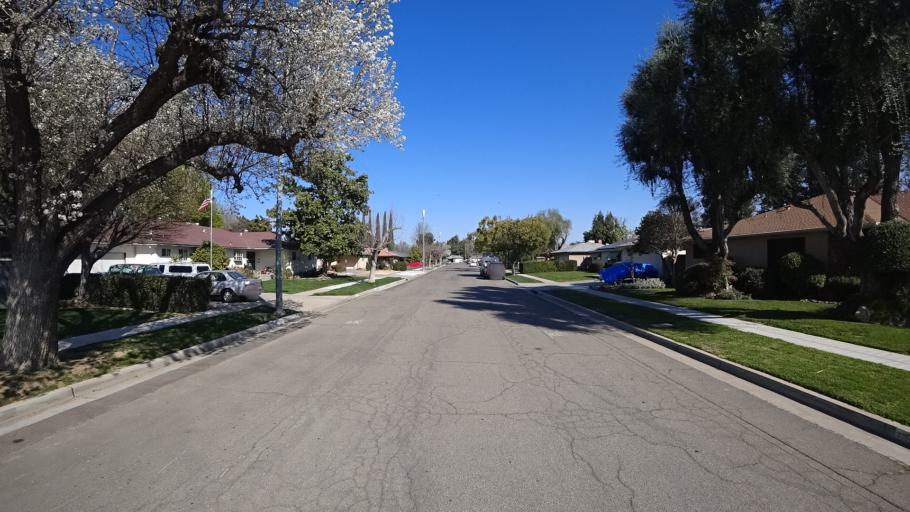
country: US
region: California
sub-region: Fresno County
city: Clovis
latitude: 36.8284
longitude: -119.7563
